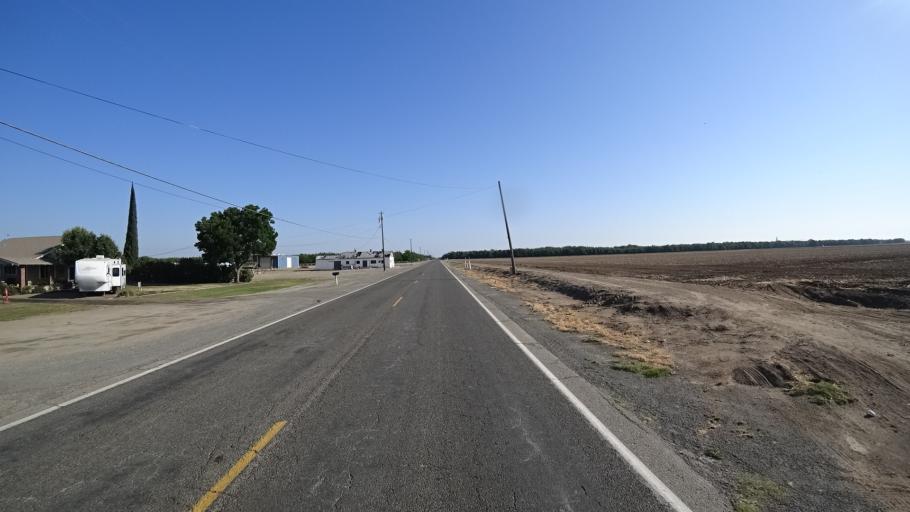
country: US
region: California
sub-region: Kings County
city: Lucerne
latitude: 36.3752
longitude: -119.7090
